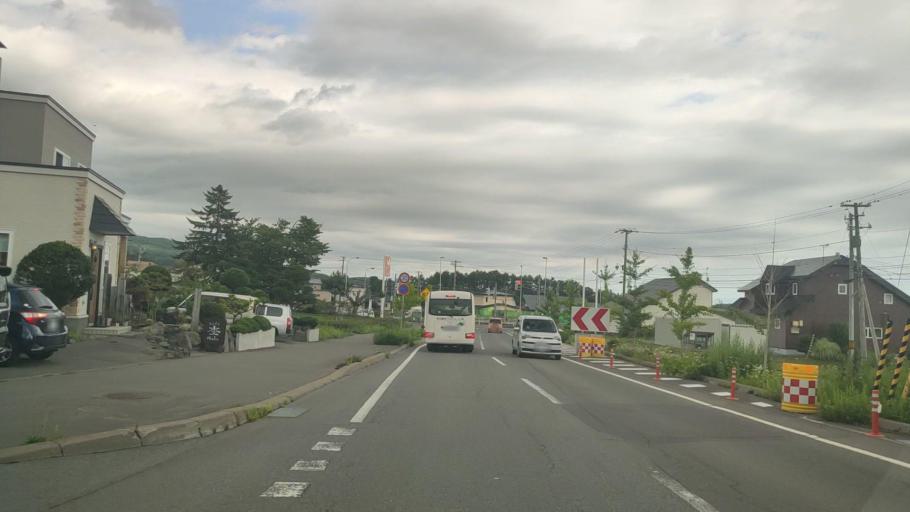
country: JP
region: Hokkaido
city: Date
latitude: 42.5496
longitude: 140.7704
